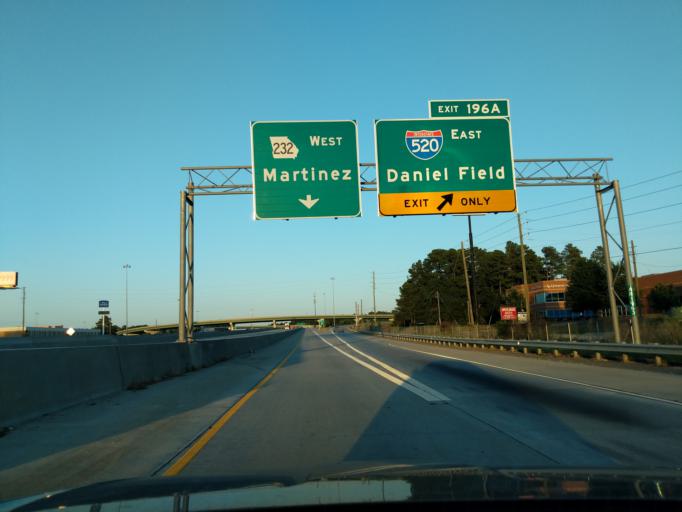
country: US
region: Georgia
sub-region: Columbia County
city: Martinez
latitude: 33.4916
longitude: -82.0903
